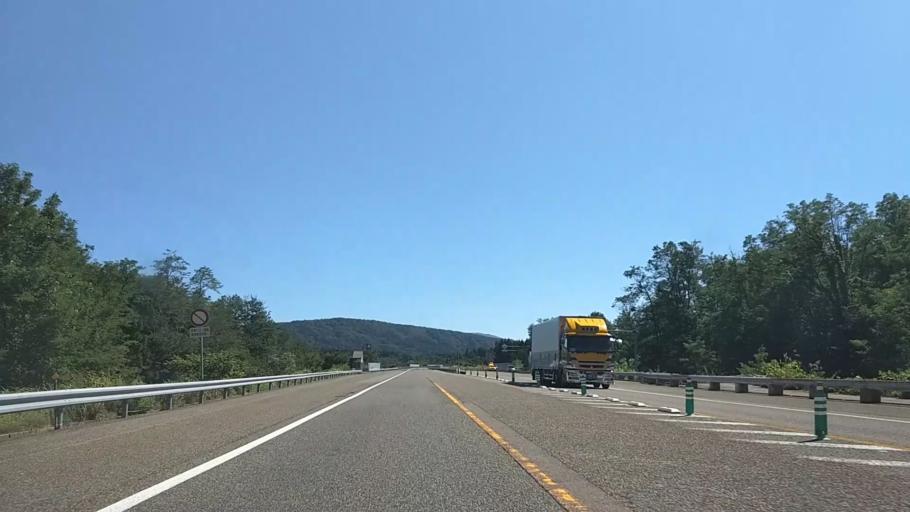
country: JP
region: Niigata
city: Arai
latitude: 36.9828
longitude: 138.2167
